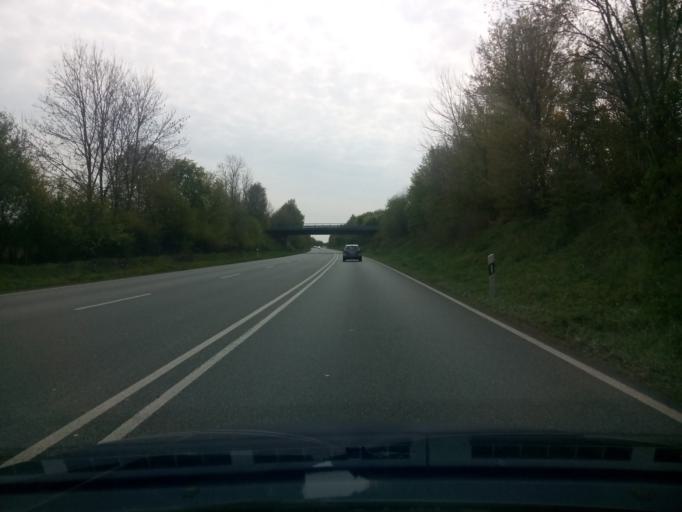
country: DE
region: Lower Saxony
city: Stuhr
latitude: 53.0143
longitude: 8.7983
